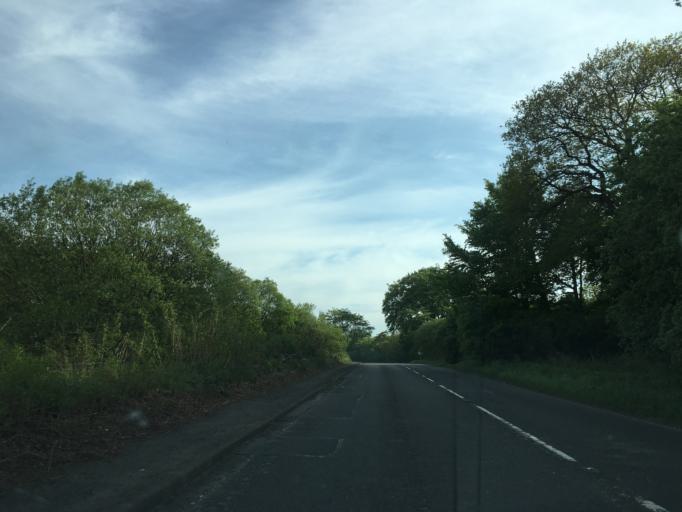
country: GB
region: Scotland
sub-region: Midlothian
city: Penicuik
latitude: 55.8134
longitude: -3.2294
